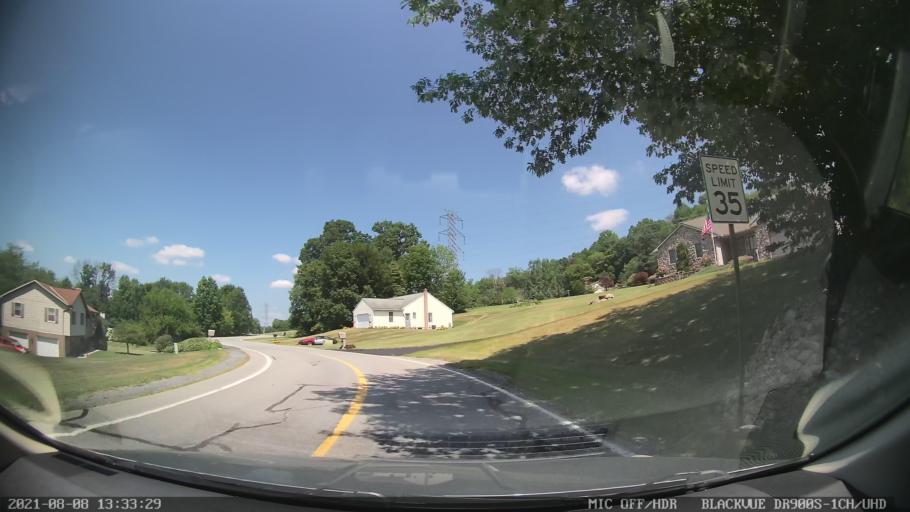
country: US
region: Pennsylvania
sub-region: Berks County
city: Fleetwood
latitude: 40.4452
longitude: -75.7614
